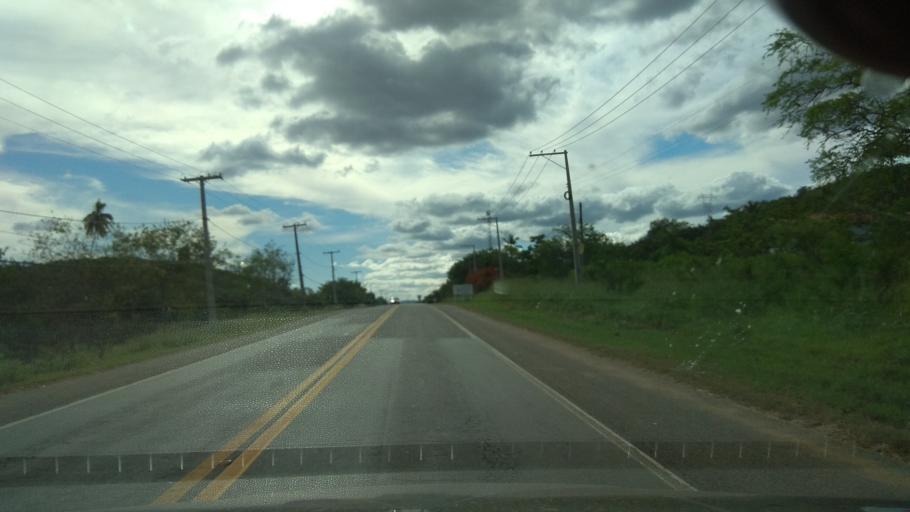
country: BR
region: Bahia
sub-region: Jequie
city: Jequie
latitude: -13.8783
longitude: -40.0365
